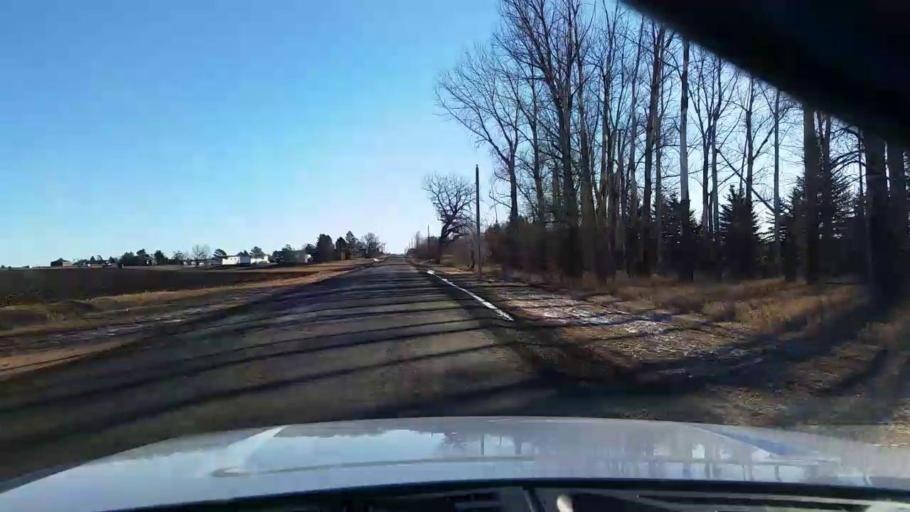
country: US
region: Colorado
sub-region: Larimer County
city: Wellington
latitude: 40.7695
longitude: -105.0908
